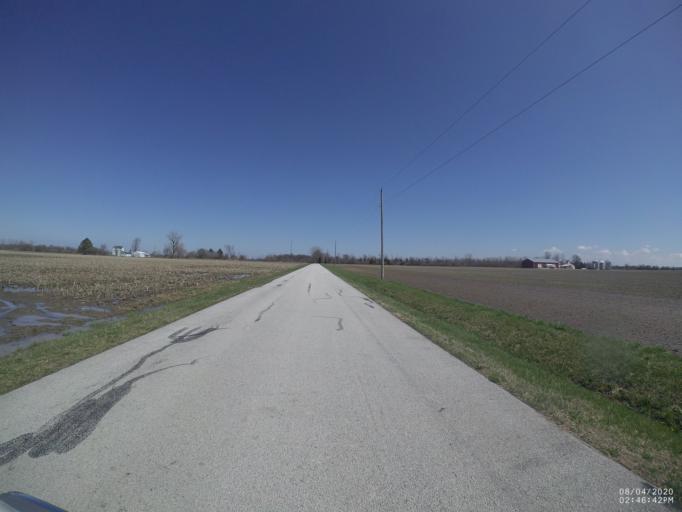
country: US
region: Ohio
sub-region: Sandusky County
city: Gibsonburg
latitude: 41.2974
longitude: -83.2776
